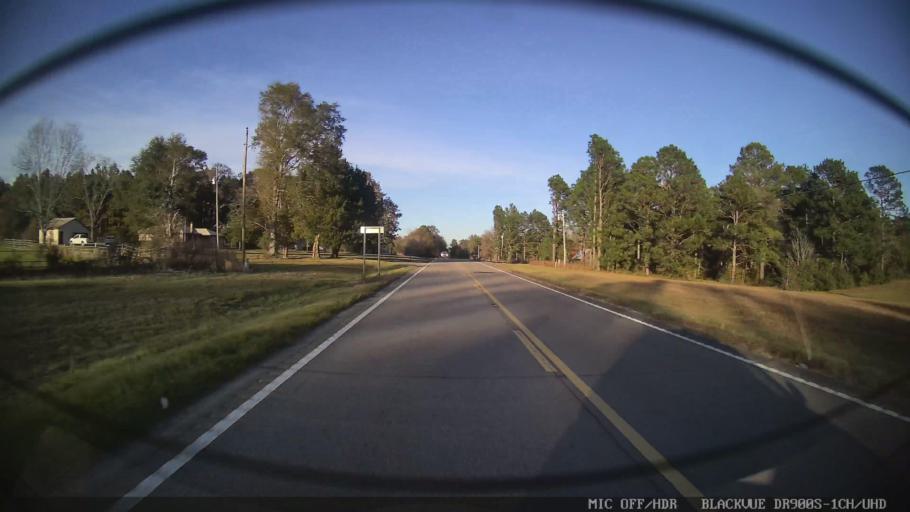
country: US
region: Mississippi
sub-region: Lamar County
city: Lumberton
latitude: 31.0400
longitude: -89.4387
